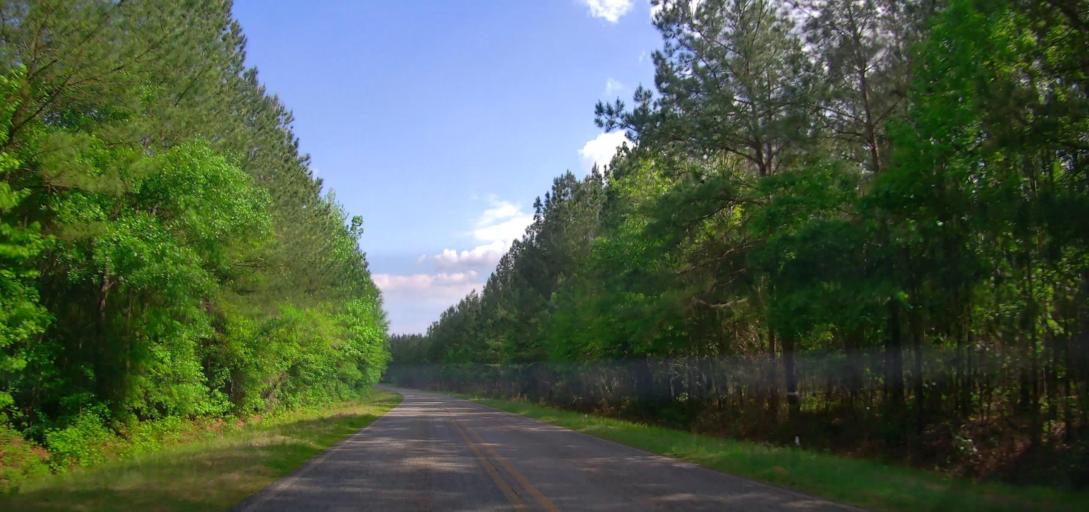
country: US
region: Georgia
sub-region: Laurens County
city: East Dublin
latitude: 32.7031
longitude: -82.9164
